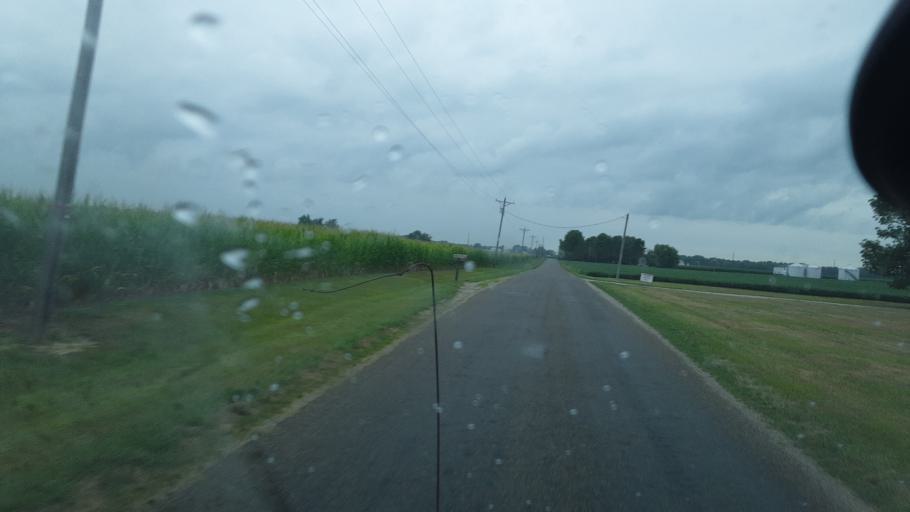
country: US
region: Ohio
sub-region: Defiance County
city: Hicksville
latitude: 41.3336
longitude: -84.6698
